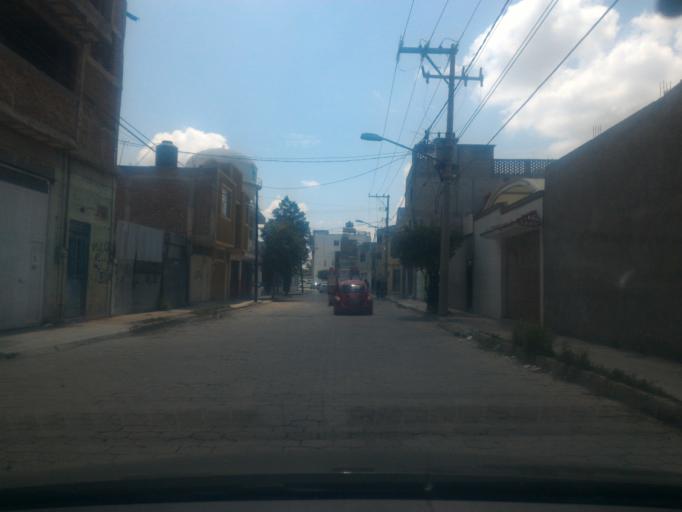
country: MX
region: Guanajuato
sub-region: Purisima del Rincon
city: Monte Grande
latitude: 21.0085
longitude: -101.8608
